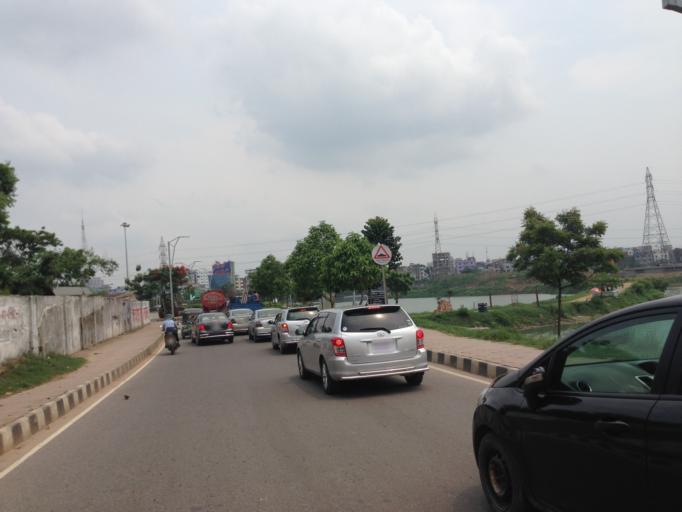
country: BD
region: Dhaka
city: Paltan
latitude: 23.7725
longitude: 90.4182
